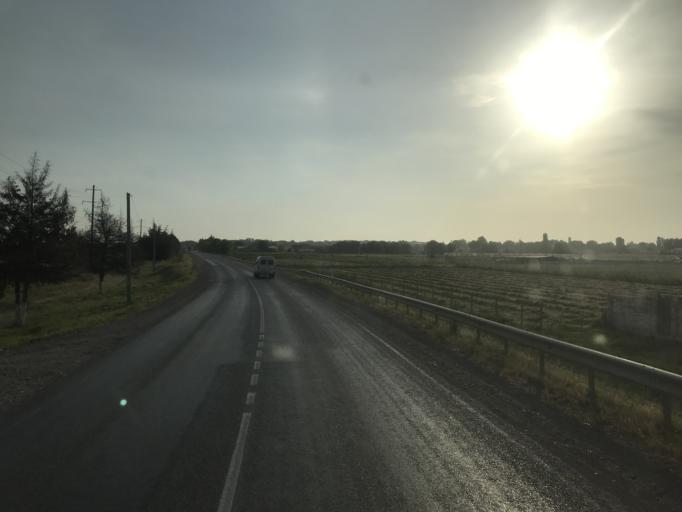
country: KZ
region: Ongtustik Qazaqstan
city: Saryaghash
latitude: 41.4831
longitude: 69.2525
